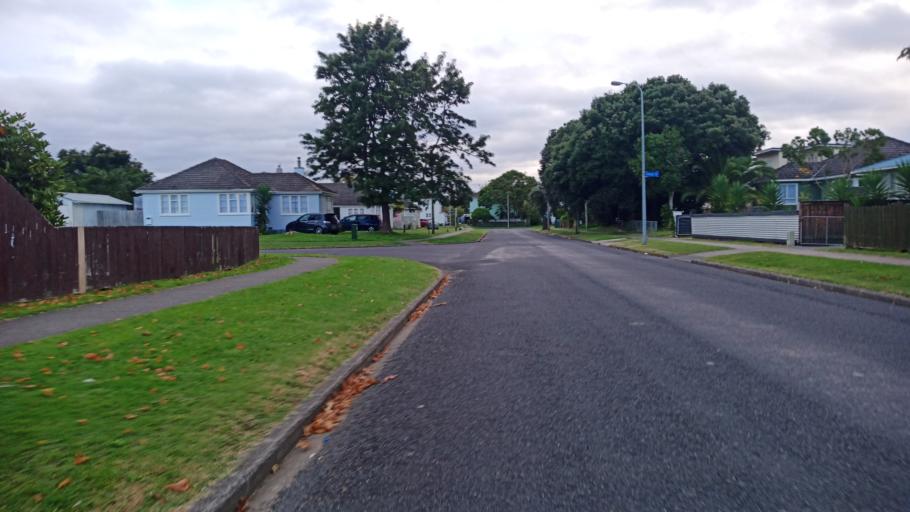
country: NZ
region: Gisborne
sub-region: Gisborne District
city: Gisborne
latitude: -38.6576
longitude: 178.0008
